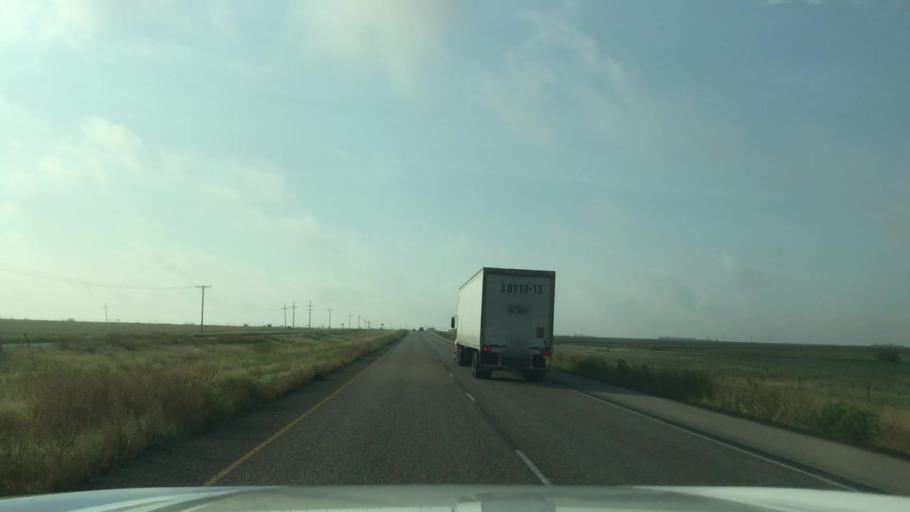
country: US
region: Texas
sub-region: Garza County
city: Post
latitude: 33.2505
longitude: -101.4652
